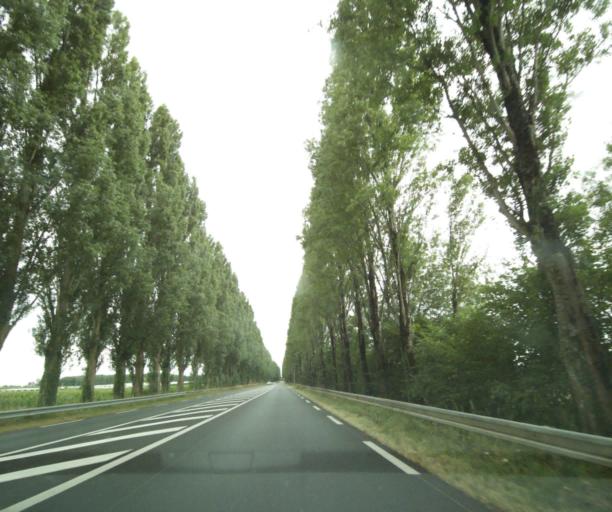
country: FR
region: Pays de la Loire
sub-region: Departement de Maine-et-Loire
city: Corze
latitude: 47.5407
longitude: -0.4031
